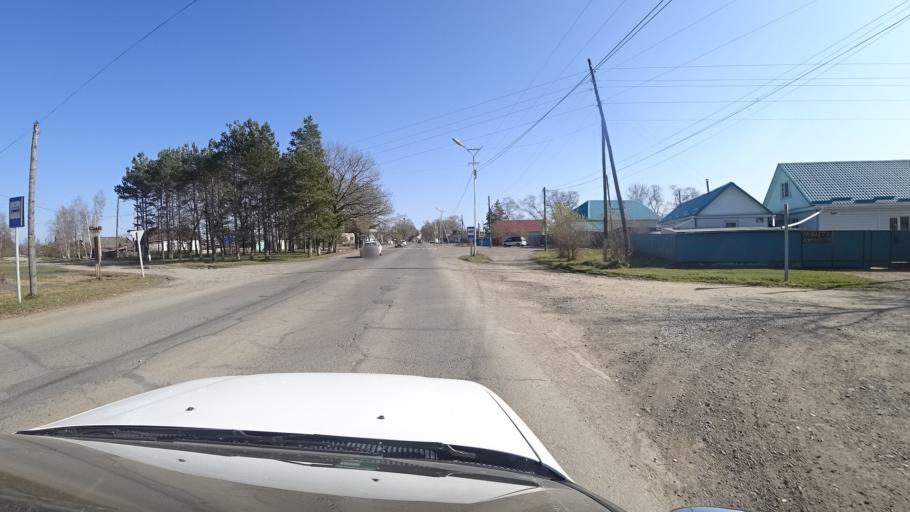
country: RU
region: Primorskiy
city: Dal'nerechensk
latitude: 45.9254
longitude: 133.7398
